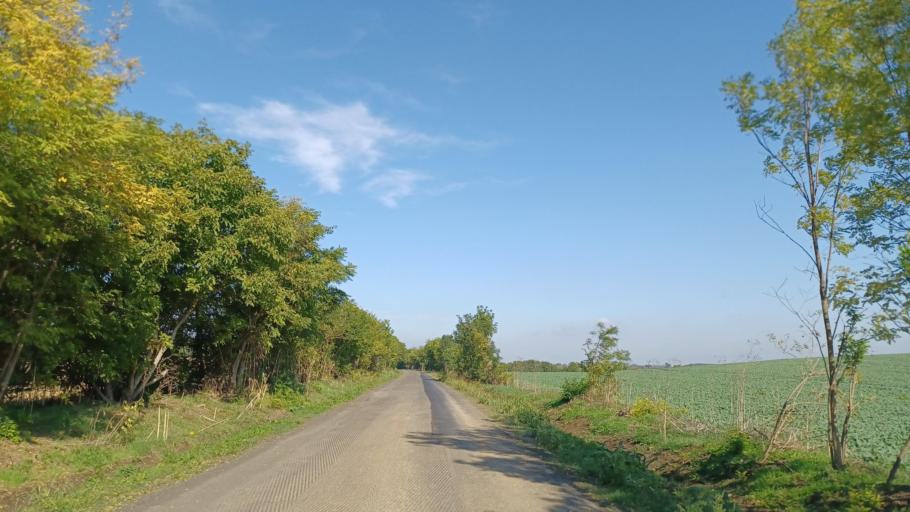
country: HU
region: Tolna
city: Nagydorog
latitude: 46.5884
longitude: 18.5965
